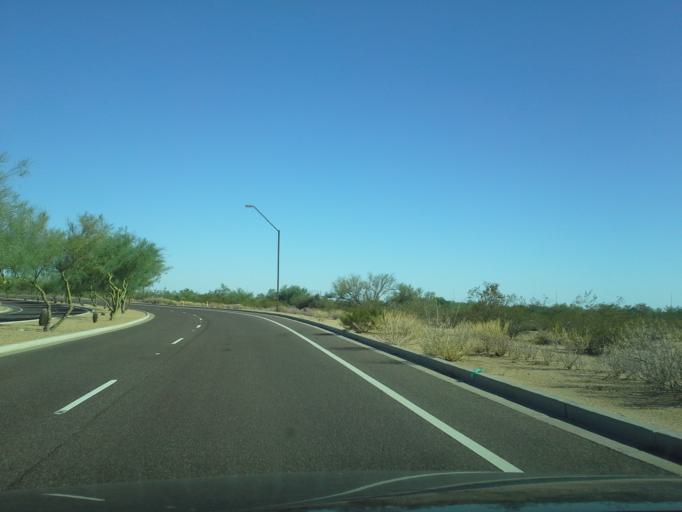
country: US
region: Arizona
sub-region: Maricopa County
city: Paradise Valley
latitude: 33.6627
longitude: -111.9204
